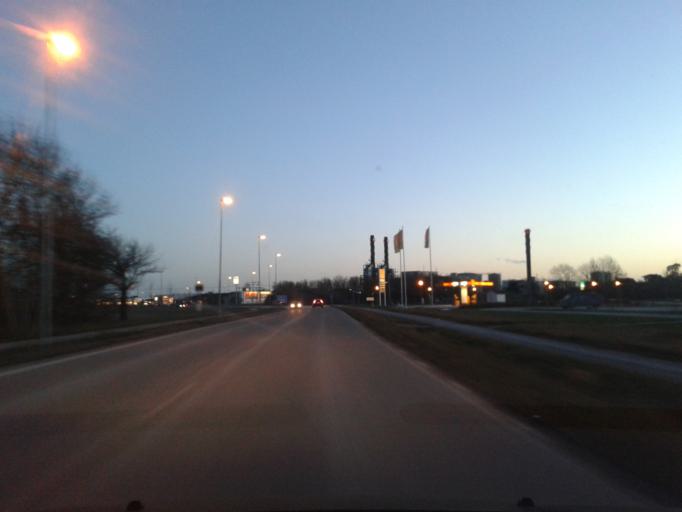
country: SE
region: Gotland
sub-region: Gotland
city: Visby
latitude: 57.6277
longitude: 18.3178
